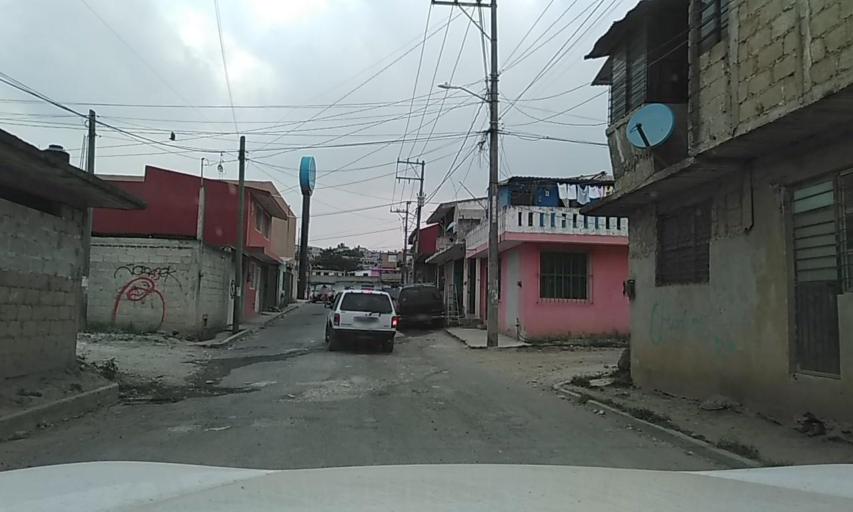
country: MX
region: Veracruz
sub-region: Jilotepec
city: El Pueblito (Garbanzal)
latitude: 19.5695
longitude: -96.8997
